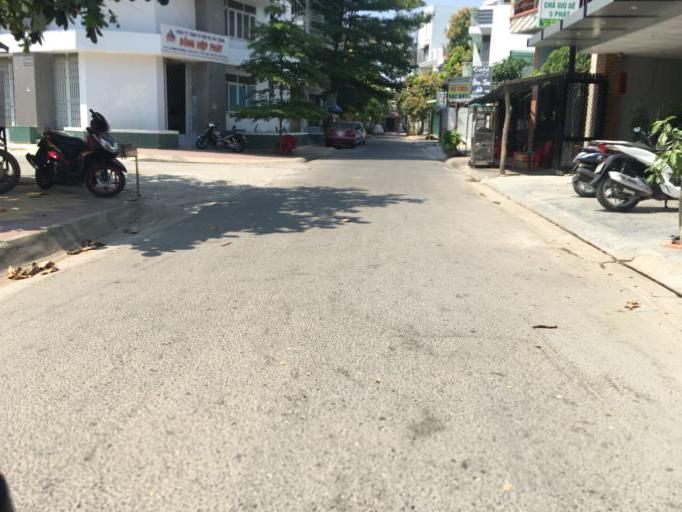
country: VN
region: Ninh Thuan
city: Phan Rang-Thap Cham
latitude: 11.5690
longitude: 108.9938
